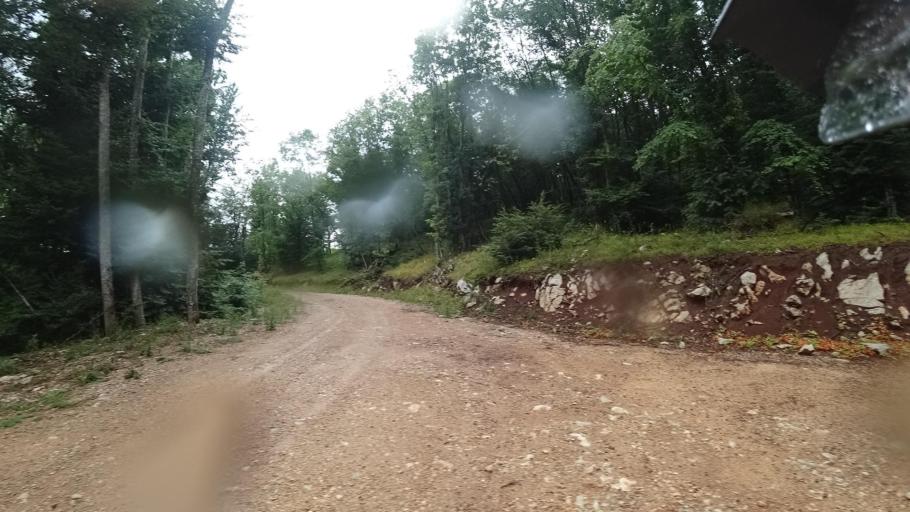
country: HR
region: Licko-Senjska
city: Jezerce
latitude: 44.7112
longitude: 15.6588
